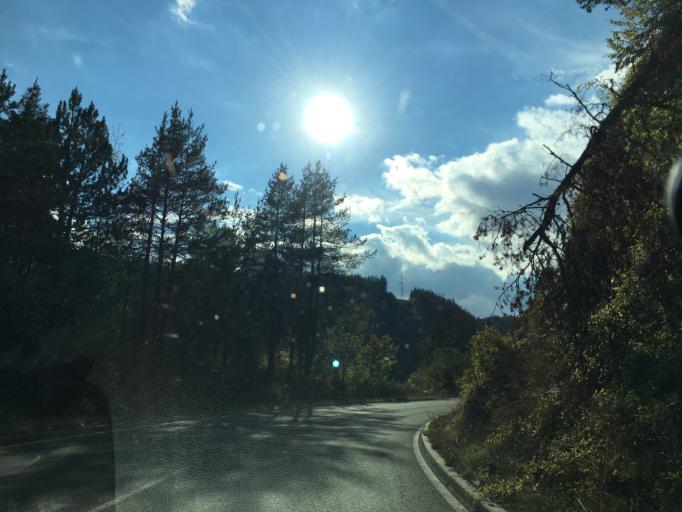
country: BG
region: Smolyan
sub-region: Obshtina Madan
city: Madan
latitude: 41.5395
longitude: 24.9159
